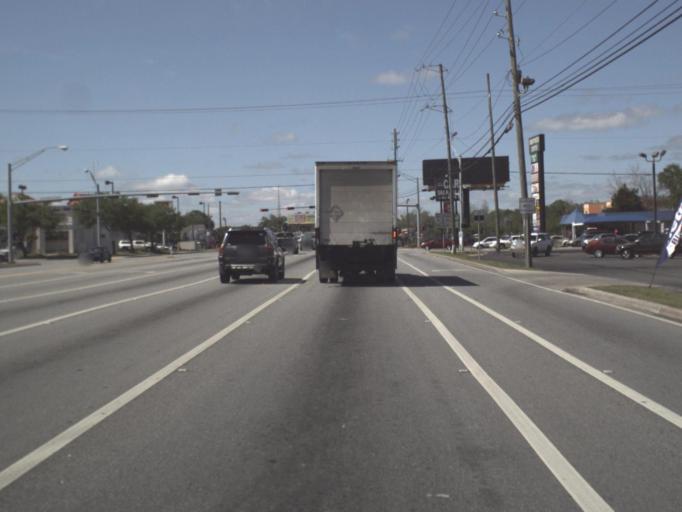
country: US
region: Florida
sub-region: Escambia County
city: Brent
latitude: 30.4658
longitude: -87.2419
